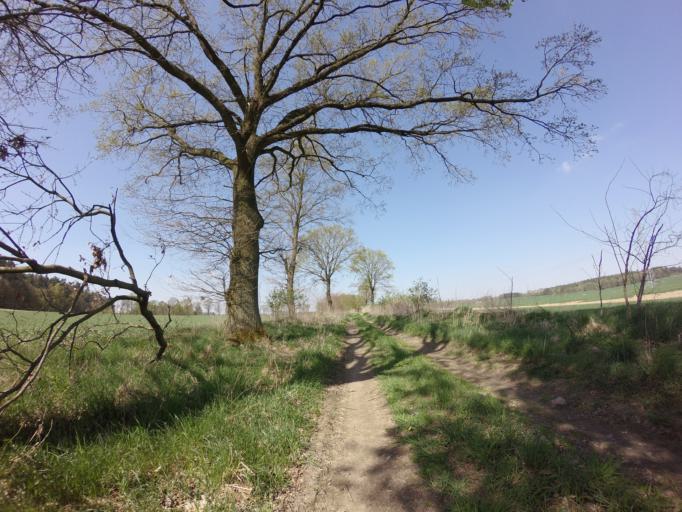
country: PL
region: West Pomeranian Voivodeship
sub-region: Powiat choszczenski
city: Choszczno
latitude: 53.2098
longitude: 15.3580
